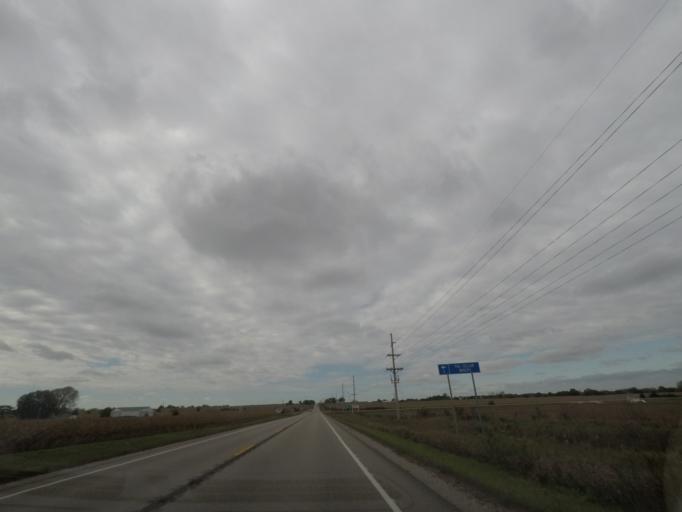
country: US
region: Iowa
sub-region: Story County
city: Huxley
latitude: 41.8778
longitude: -93.5287
